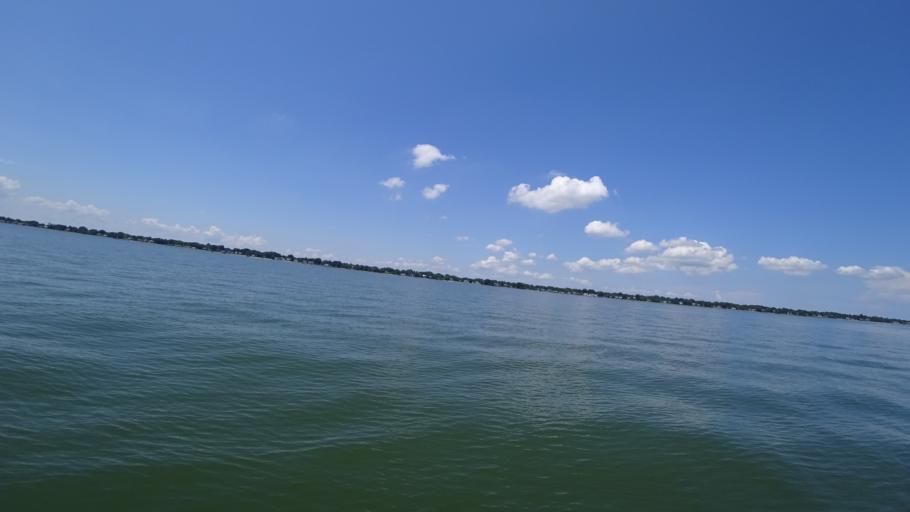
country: US
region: Virginia
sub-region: City of Hampton
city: Hampton
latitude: 36.9862
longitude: -76.3694
